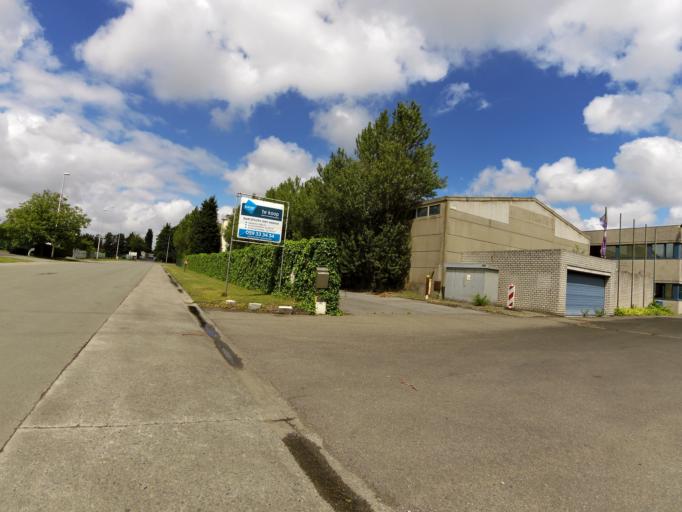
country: BE
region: Flanders
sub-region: Provincie West-Vlaanderen
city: Gistel
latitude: 51.1498
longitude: 2.9449
